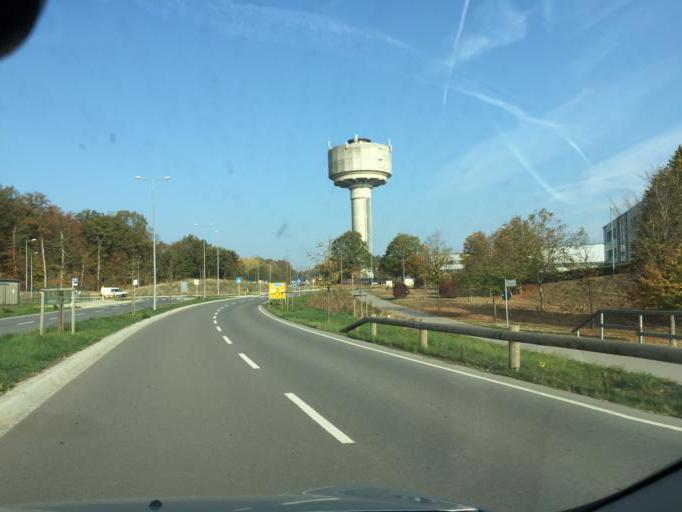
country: LU
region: Luxembourg
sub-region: Canton de Luxembourg
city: Contern
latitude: 49.5952
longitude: 6.2148
